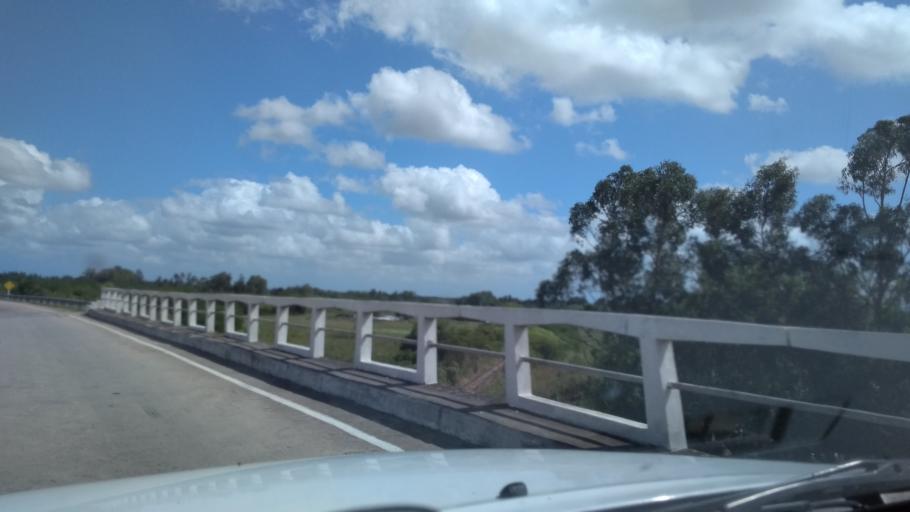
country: UY
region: Canelones
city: Sauce
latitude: -34.6392
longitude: -56.0527
